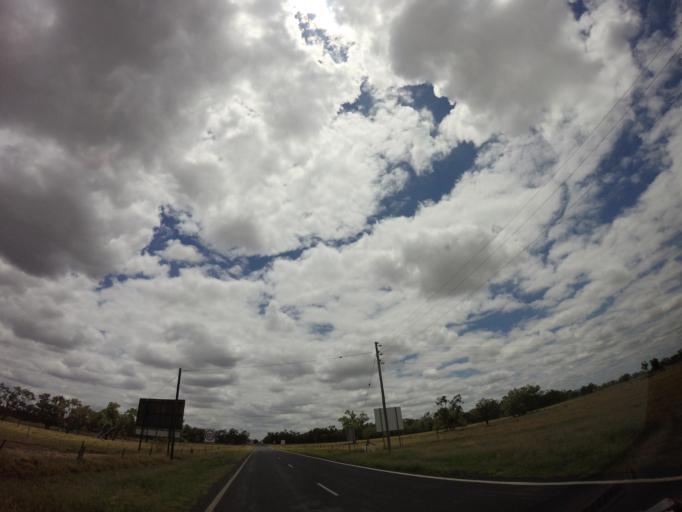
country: AU
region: Queensland
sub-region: Goondiwindi
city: Goondiwindi
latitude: -28.5115
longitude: 150.2896
